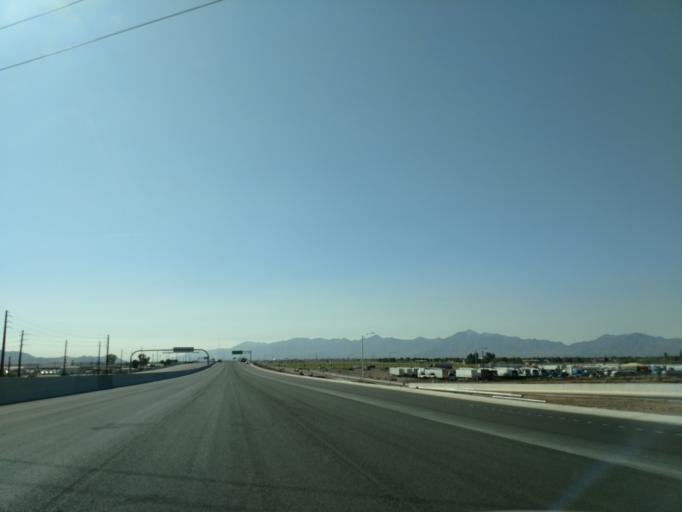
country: US
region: Arizona
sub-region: Maricopa County
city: Tolleson
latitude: 33.4411
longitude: -112.1873
